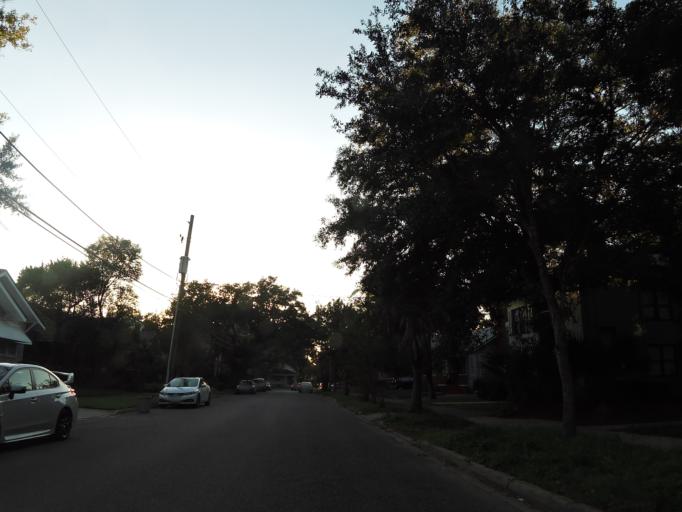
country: US
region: Florida
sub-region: Duval County
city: Jacksonville
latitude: 30.3158
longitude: -81.6958
